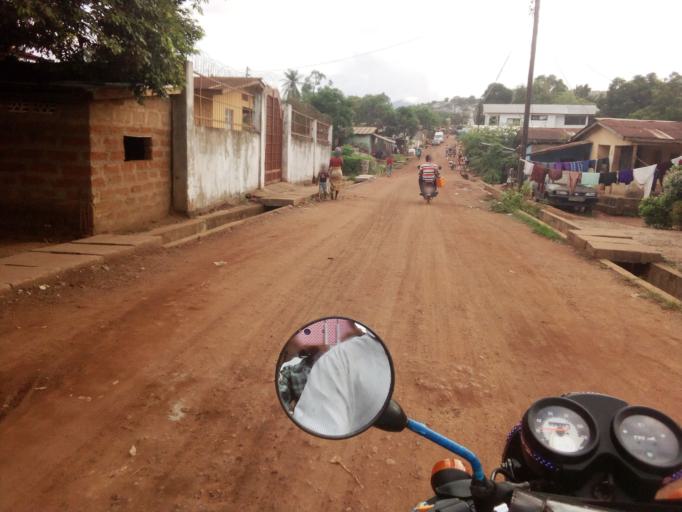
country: SL
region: Western Area
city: Waterloo
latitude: 8.3400
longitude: -13.0720
